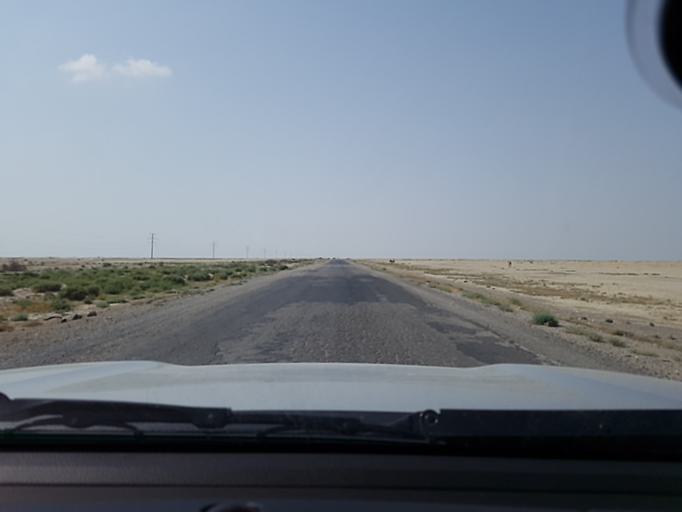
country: TM
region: Balkan
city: Gumdag
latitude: 38.8956
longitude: 54.5926
